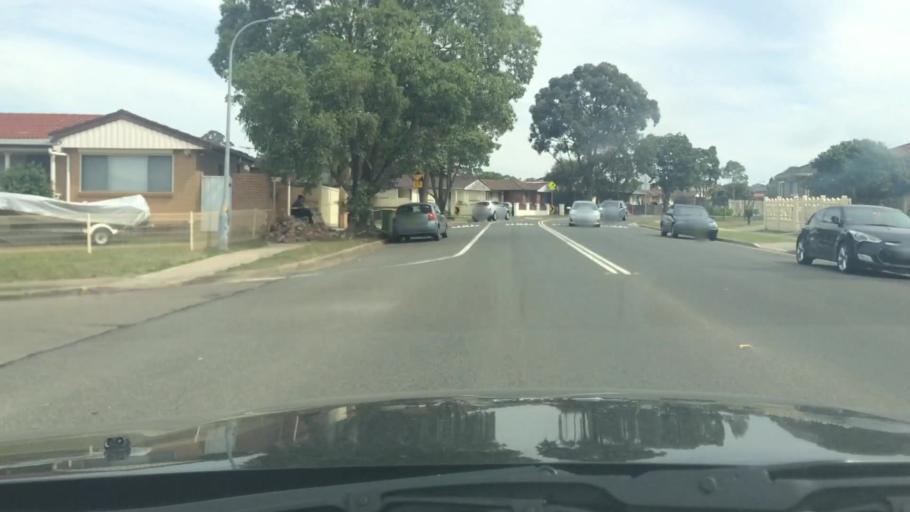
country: AU
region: New South Wales
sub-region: Fairfield
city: Cabramatta West
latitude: -33.8668
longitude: 150.8953
